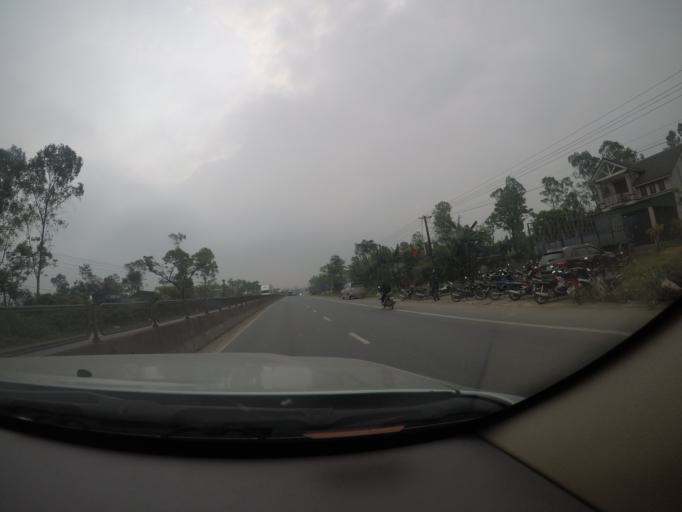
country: VN
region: Ha Tinh
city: Cam Xuyen
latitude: 18.2040
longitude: 106.1440
